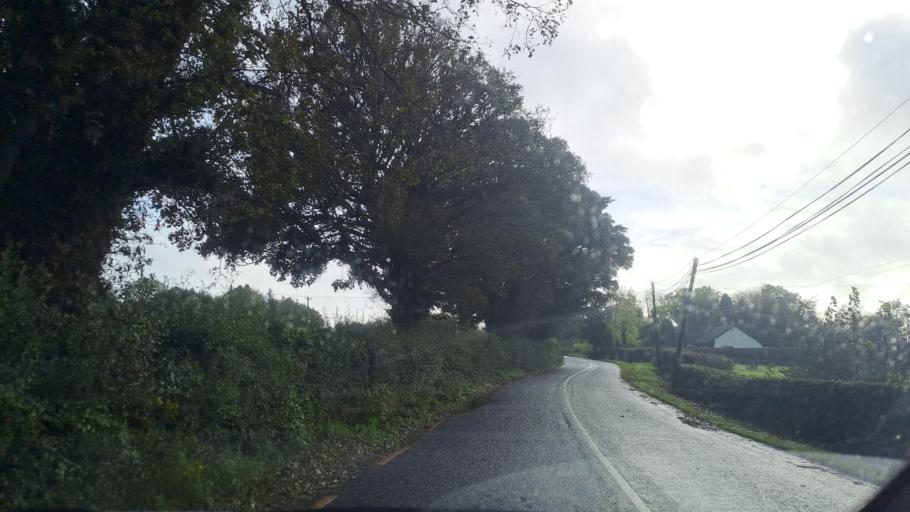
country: IE
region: Ulster
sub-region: County Monaghan
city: Carrickmacross
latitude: 53.9402
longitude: -6.7173
